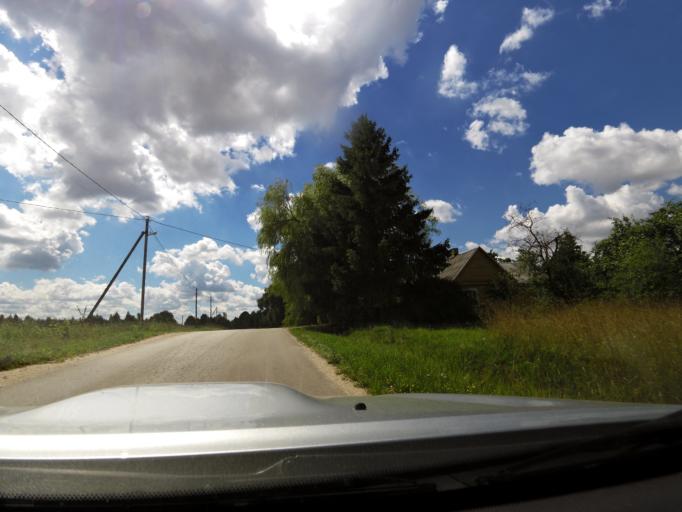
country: LT
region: Vilnius County
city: Elektrenai
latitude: 54.9123
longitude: 24.6509
